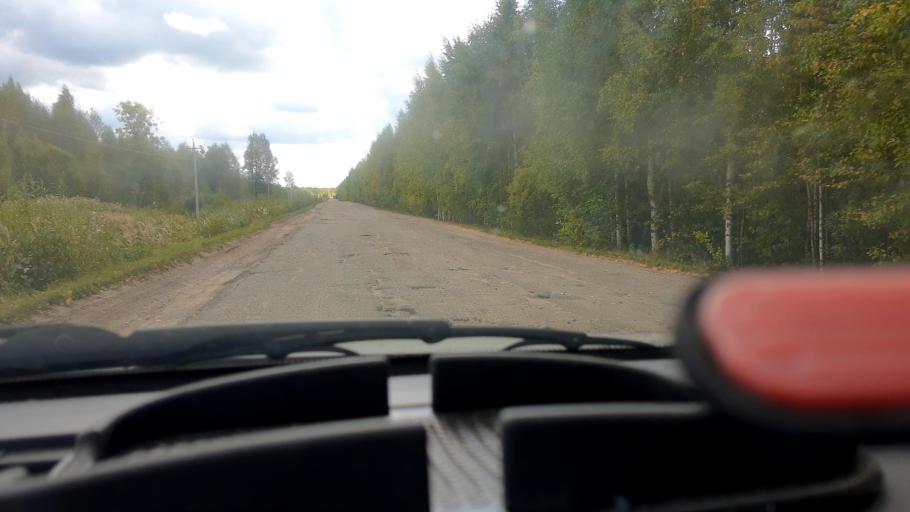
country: RU
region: Mariy-El
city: Kilemary
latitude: 56.8916
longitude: 46.7550
